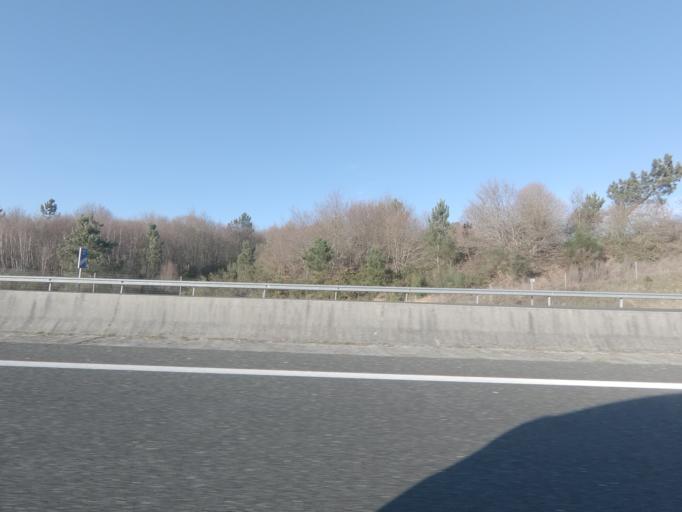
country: ES
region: Galicia
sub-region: Provincia de Pontevedra
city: Lalin
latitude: 42.6711
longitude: -8.1540
